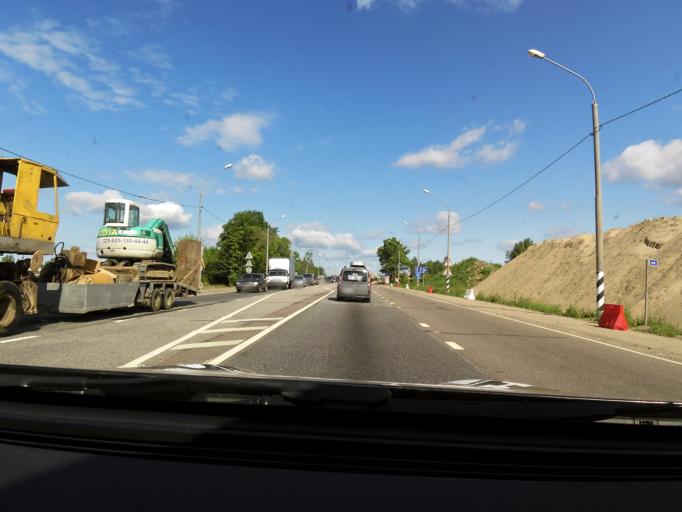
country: RU
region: Tverskaya
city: Tver
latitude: 56.8254
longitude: 35.8135
